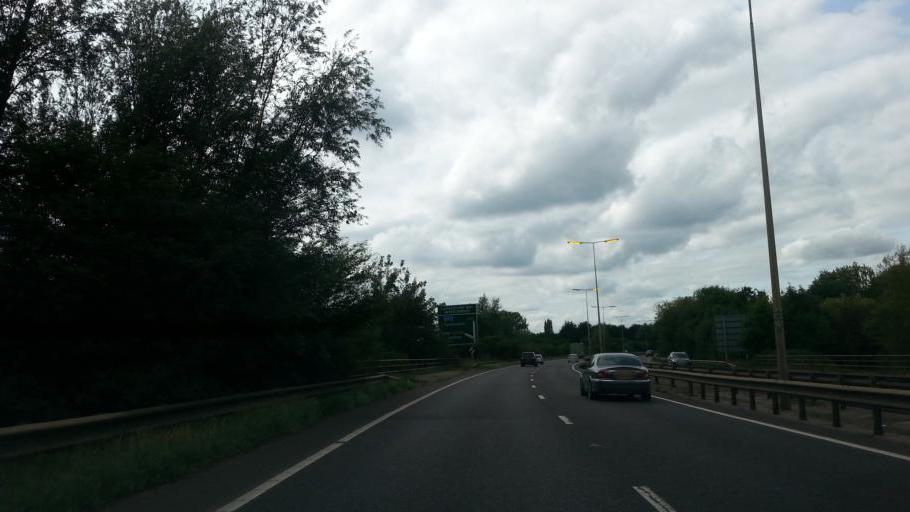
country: GB
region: England
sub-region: Northamptonshire
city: Northampton
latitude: 52.2467
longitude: -0.8194
